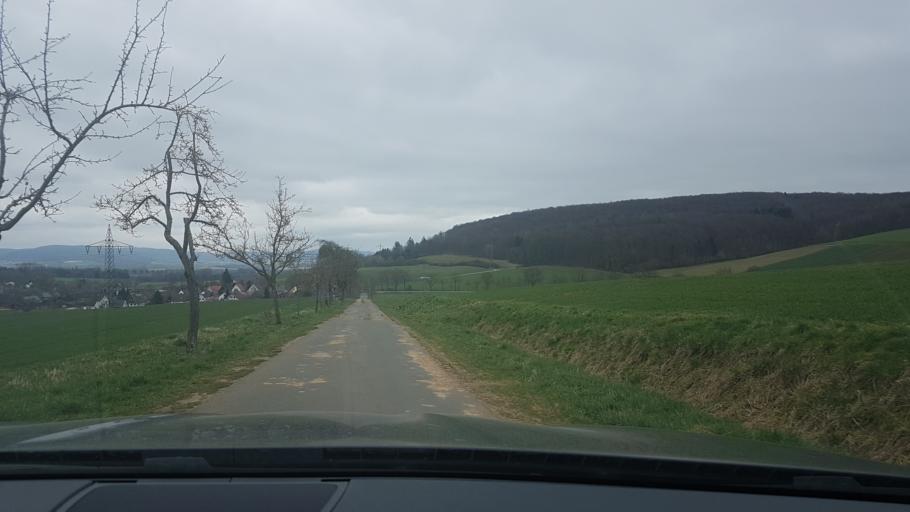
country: DE
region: Lower Saxony
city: Hameln
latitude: 52.1434
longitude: 9.3833
